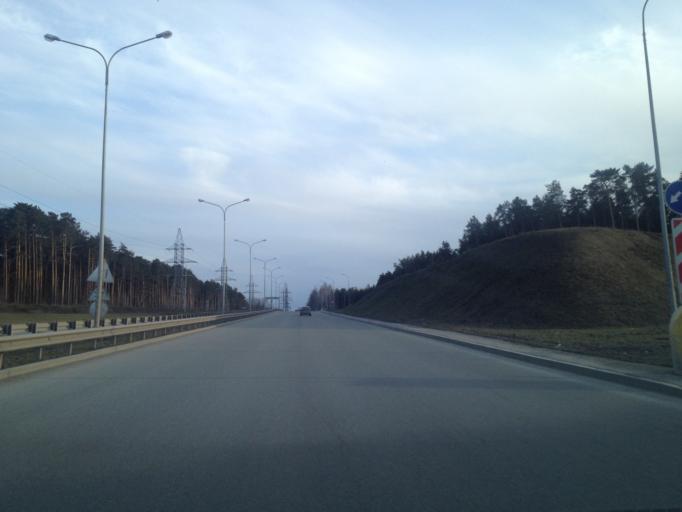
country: RU
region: Sverdlovsk
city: Sovkhoznyy
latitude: 56.7891
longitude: 60.5977
